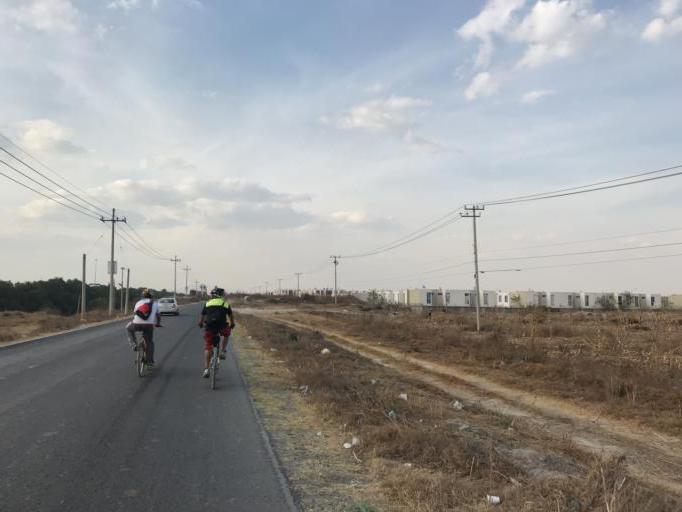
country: MX
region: Mexico
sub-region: Nextlalpan
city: Ex-Hacienda Santa Ines
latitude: 19.6949
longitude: -99.0794
